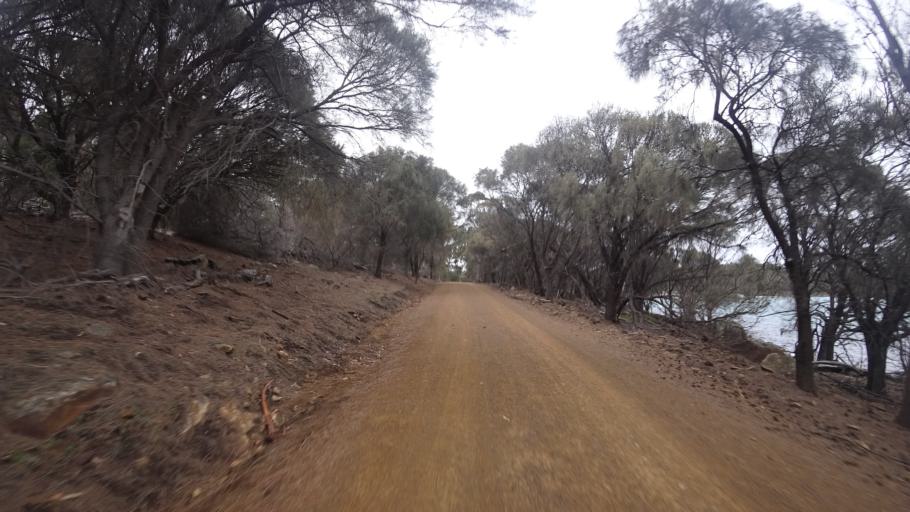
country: AU
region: Tasmania
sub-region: Sorell
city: Sorell
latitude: -42.6165
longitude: 148.0367
